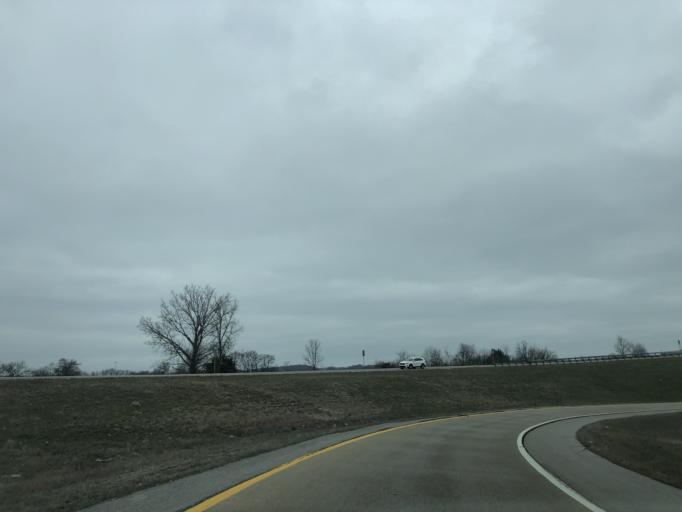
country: US
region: Tennessee
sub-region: Maury County
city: Spring Hill
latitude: 35.7391
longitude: -86.9490
